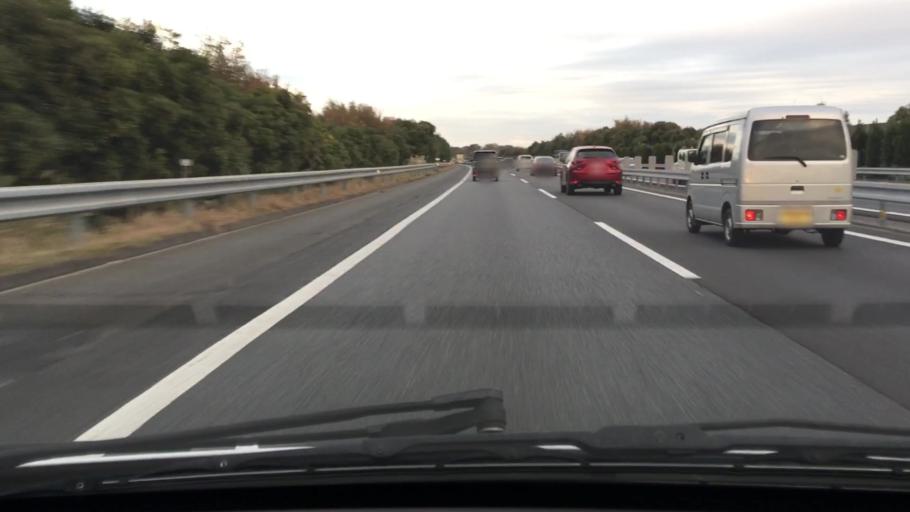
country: JP
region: Chiba
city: Ichihara
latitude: 35.5114
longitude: 140.1126
